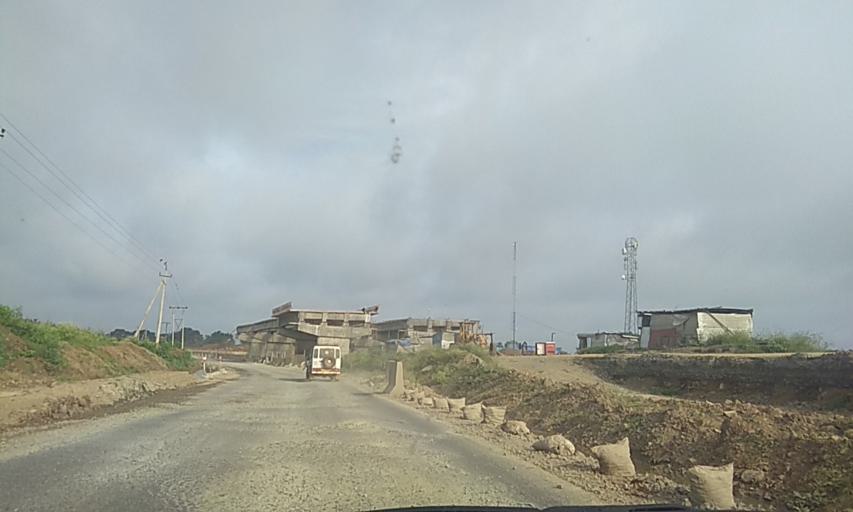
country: IN
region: Karnataka
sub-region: Haveri
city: Haveri
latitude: 14.7726
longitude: 75.4214
